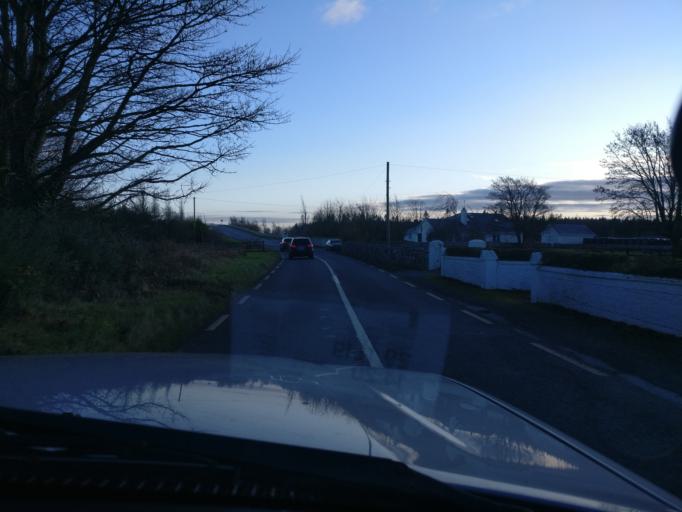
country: IE
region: Connaught
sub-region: County Galway
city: Athenry
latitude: 53.2790
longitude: -8.7211
